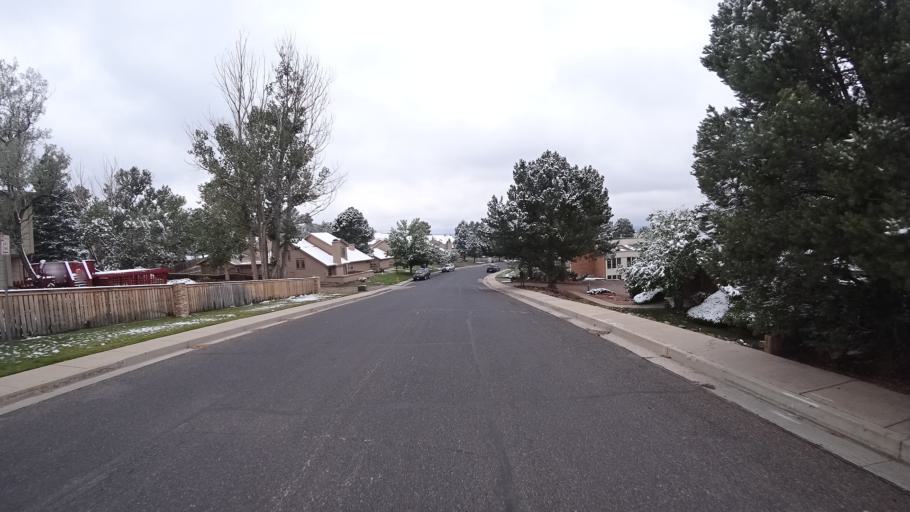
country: US
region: Colorado
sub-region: El Paso County
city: Colorado Springs
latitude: 38.9190
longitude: -104.7898
